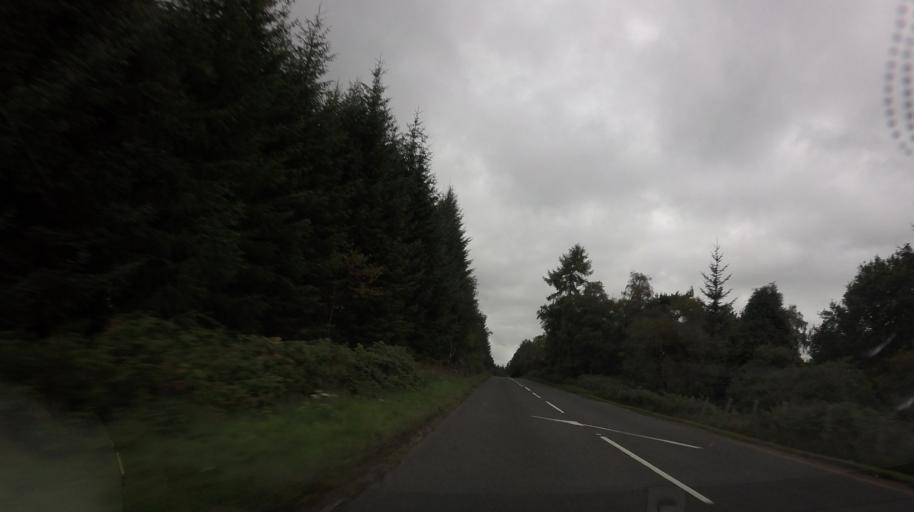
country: GB
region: Scotland
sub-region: Aberdeenshire
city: Torphins
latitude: 57.2012
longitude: -2.5934
